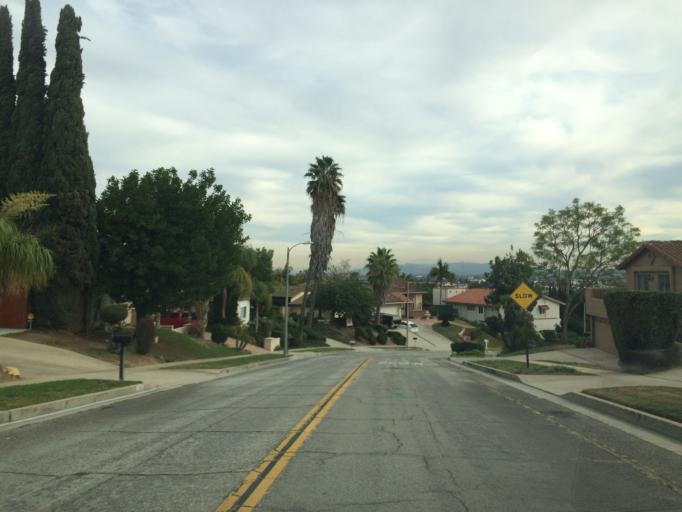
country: US
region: California
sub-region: Los Angeles County
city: South Pasadena
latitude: 34.1022
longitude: -118.1601
